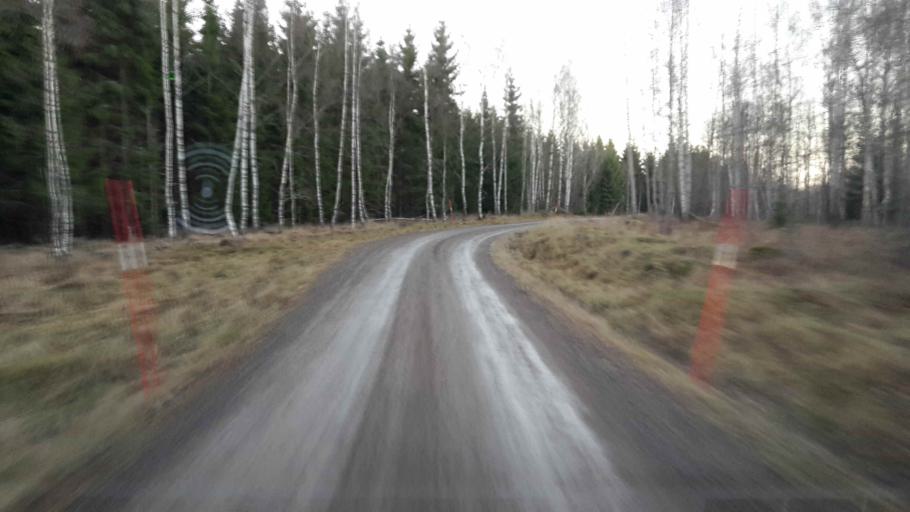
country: SE
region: OEstergoetland
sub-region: Atvidabergs Kommun
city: Atvidaberg
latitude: 58.2497
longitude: 16.0723
